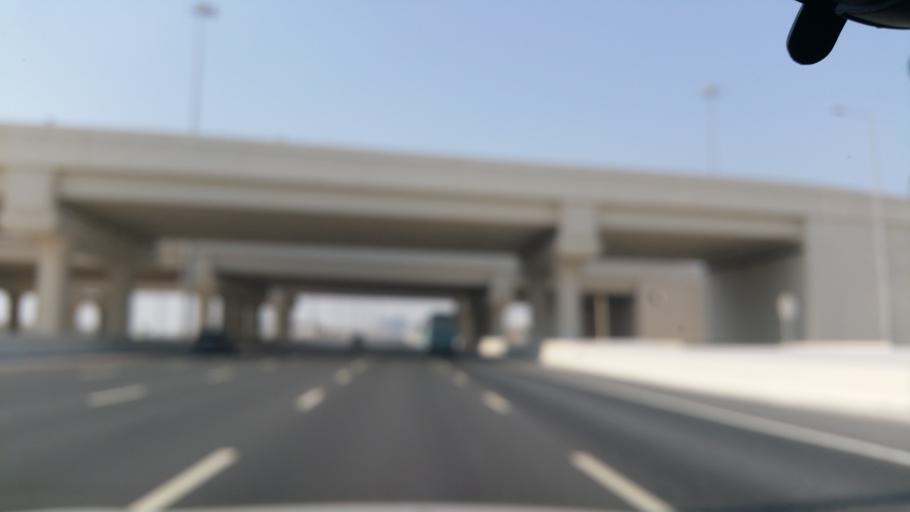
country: QA
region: Baladiyat Umm Salal
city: Umm Salal Muhammad
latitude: 25.4293
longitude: 51.4848
